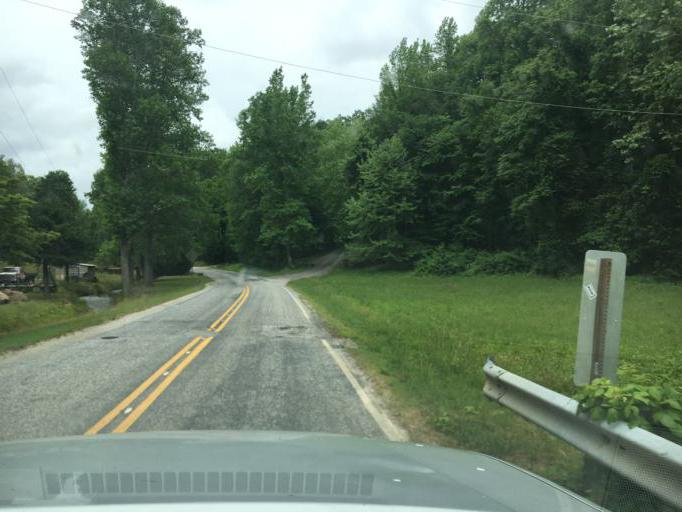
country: US
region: South Carolina
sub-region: Greenville County
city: Tigerville
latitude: 35.1333
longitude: -82.4014
